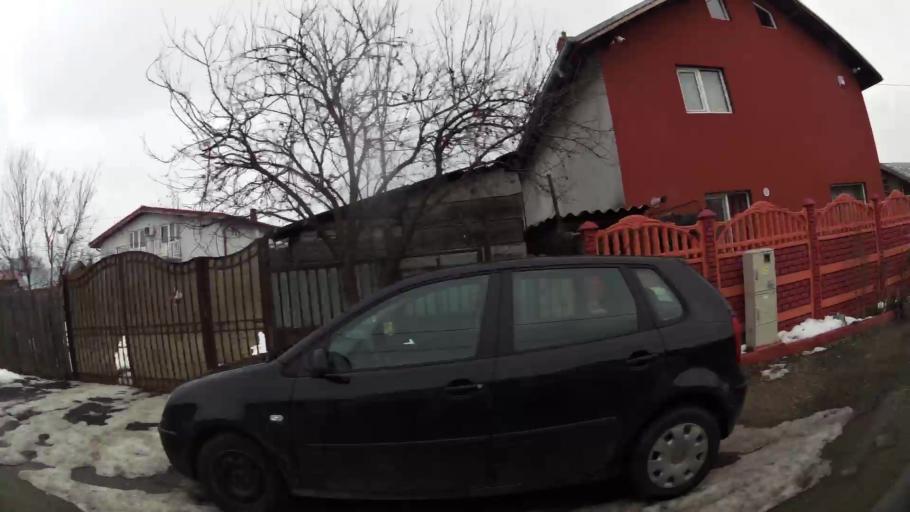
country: RO
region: Ilfov
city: Stefanestii de Jos
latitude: 44.5384
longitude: 26.2102
